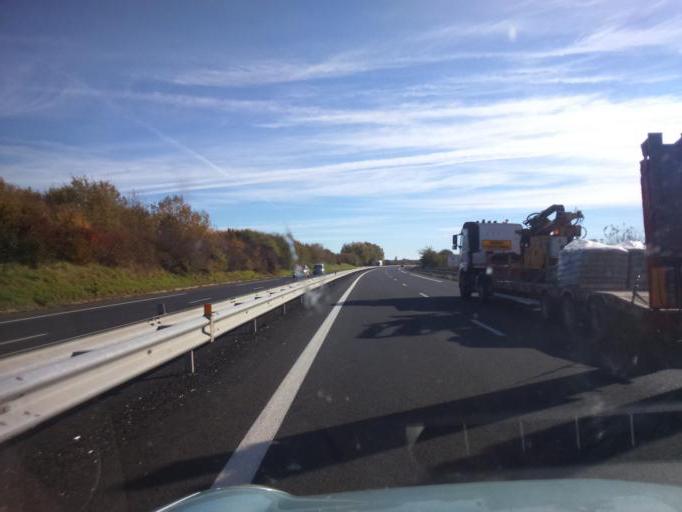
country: FR
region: Poitou-Charentes
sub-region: Departement de la Charente-Maritime
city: Tonnay-Charente
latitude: 45.9573
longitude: -0.9175
